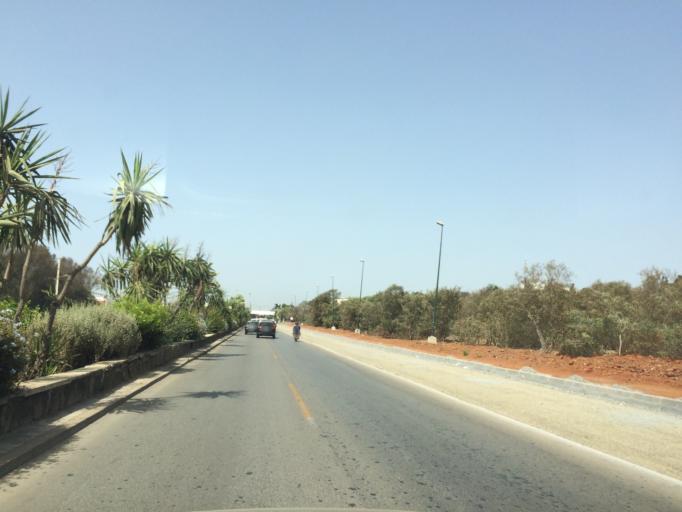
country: MA
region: Rabat-Sale-Zemmour-Zaer
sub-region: Rabat
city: Rabat
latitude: 33.9826
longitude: -6.8558
